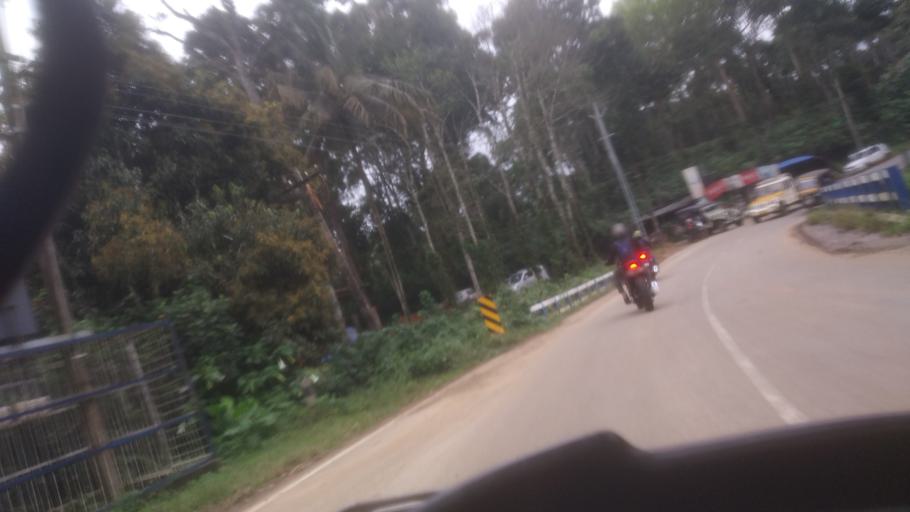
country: IN
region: Tamil Nadu
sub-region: Theni
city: Kombai
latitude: 9.8963
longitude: 77.1891
